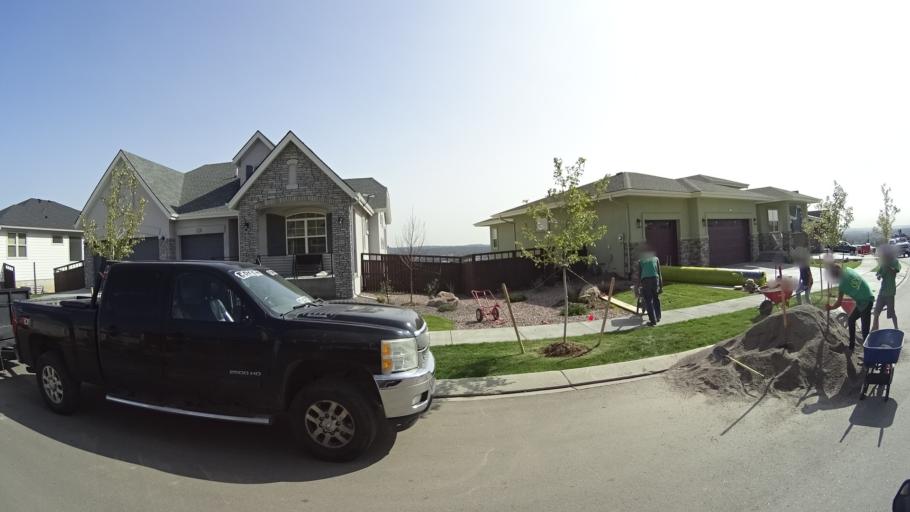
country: US
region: Colorado
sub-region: El Paso County
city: Colorado Springs
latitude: 38.8314
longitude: -104.8502
